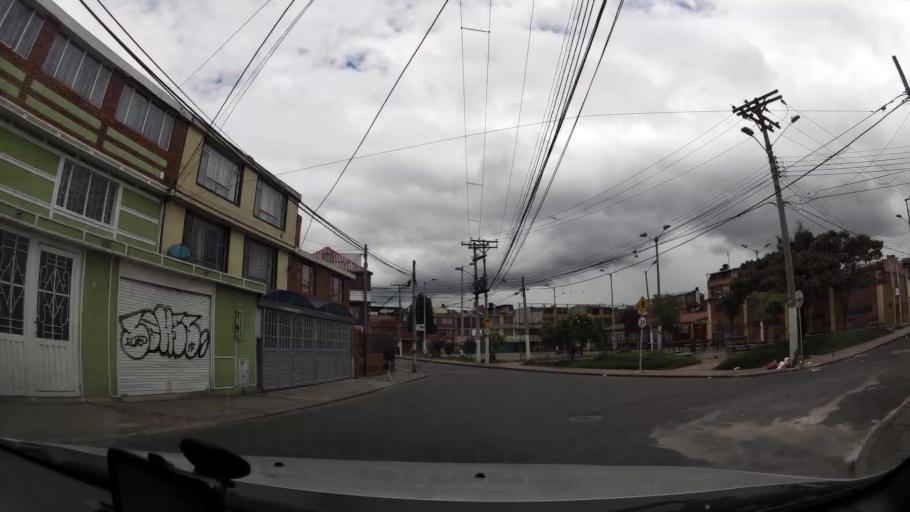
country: CO
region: Bogota D.C.
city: Bogota
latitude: 4.6024
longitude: -74.1081
